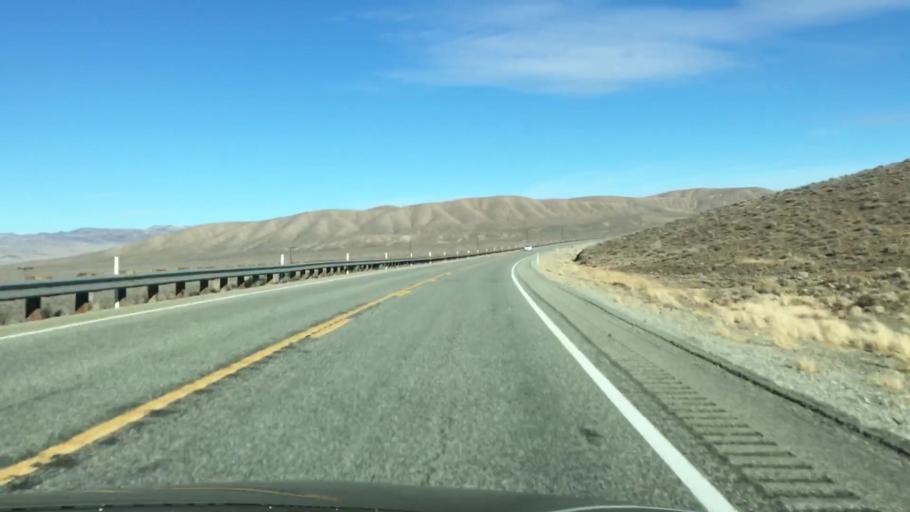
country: US
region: Nevada
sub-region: Lyon County
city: Yerington
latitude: 39.0437
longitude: -118.9811
